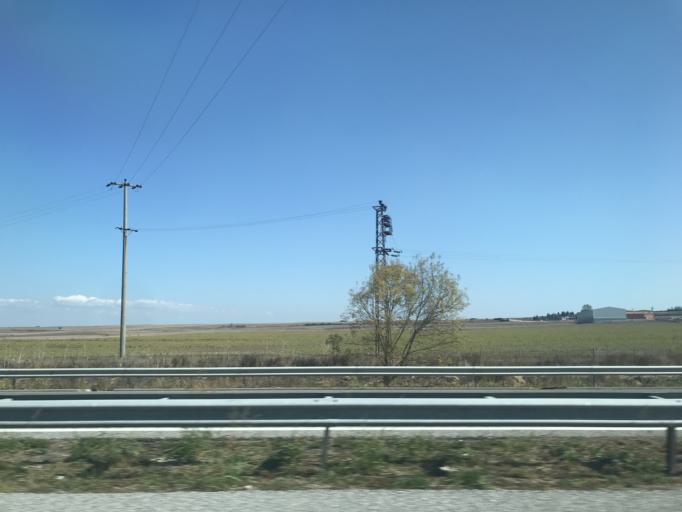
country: TR
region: Kirklareli
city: Luleburgaz
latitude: 41.4216
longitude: 27.3850
